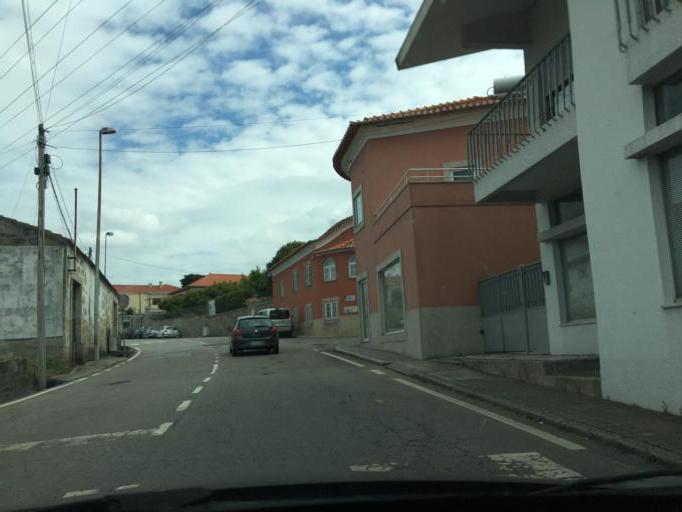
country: PT
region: Porto
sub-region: Maia
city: Maia
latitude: 41.2477
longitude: -8.6178
